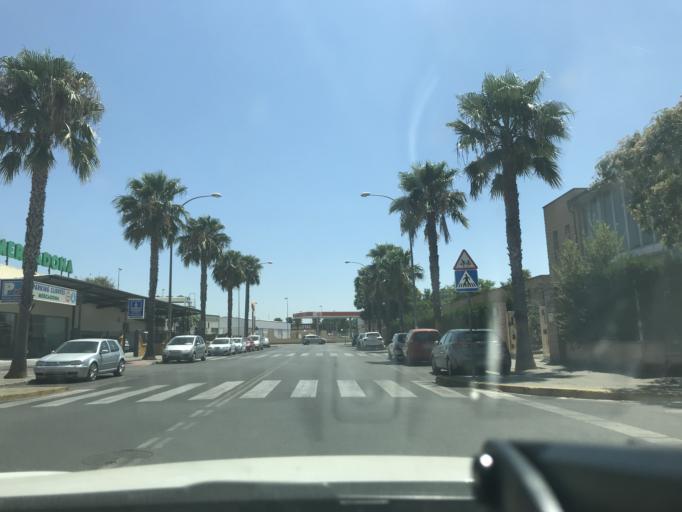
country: ES
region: Andalusia
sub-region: Provincia de Sevilla
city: La Rinconada
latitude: 37.4875
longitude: -5.9360
